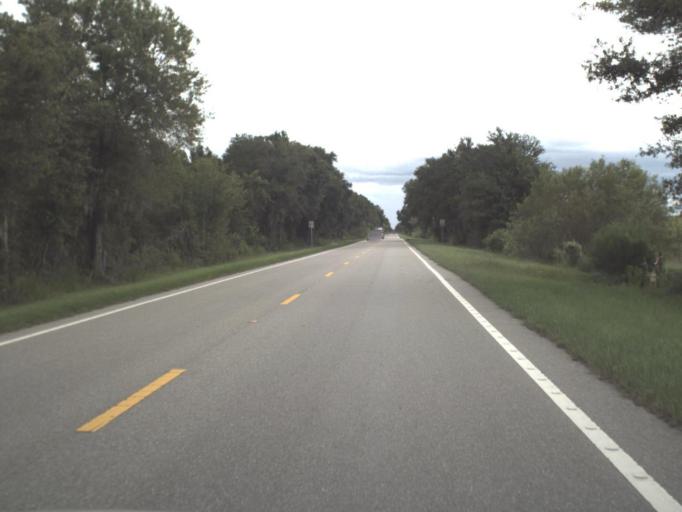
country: US
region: Florida
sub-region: Hillsborough County
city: Balm
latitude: 27.6175
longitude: -82.0877
